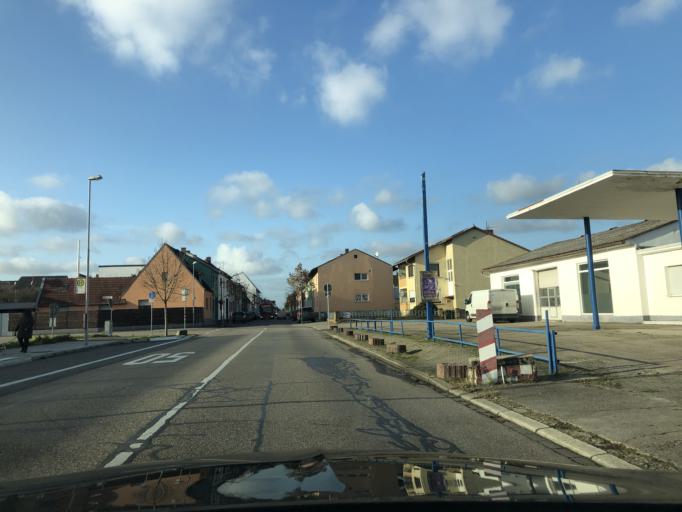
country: DE
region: Baden-Wuerttemberg
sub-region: Karlsruhe Region
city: Waghausel
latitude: 49.2397
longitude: 8.5571
